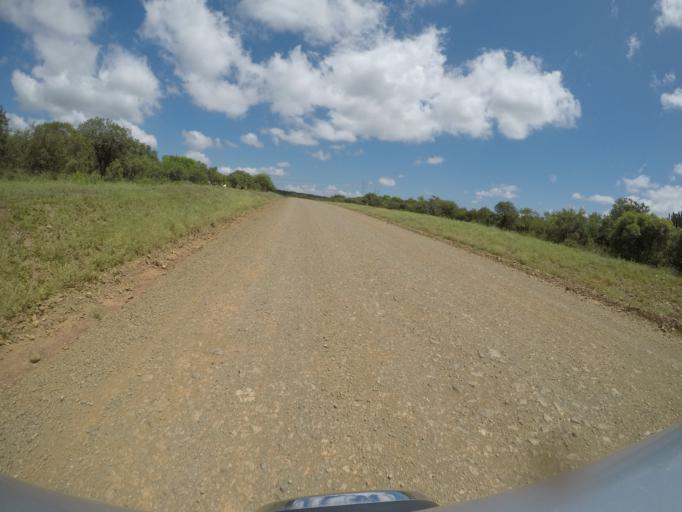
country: ZA
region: KwaZulu-Natal
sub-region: uThungulu District Municipality
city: Empangeni
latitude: -28.5994
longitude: 31.8285
